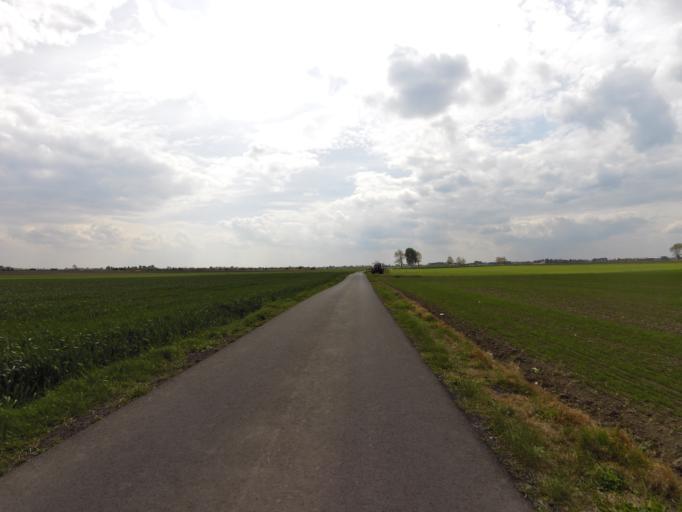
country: BE
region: Flanders
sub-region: Provincie West-Vlaanderen
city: Middelkerke
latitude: 51.1436
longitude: 2.8353
